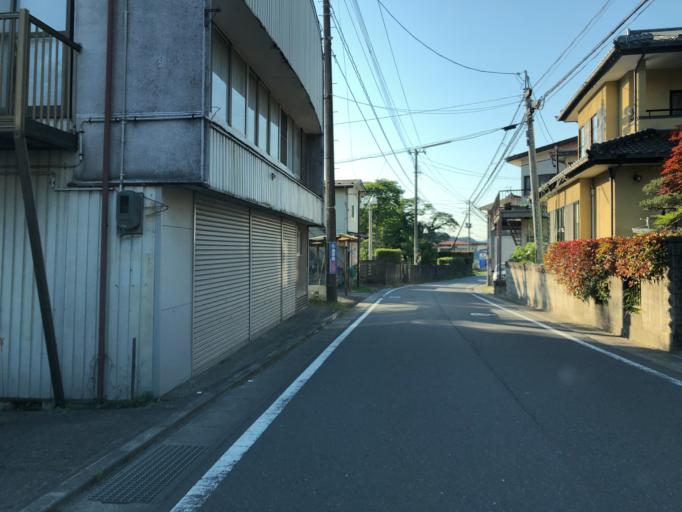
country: JP
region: Ibaraki
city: Daigo
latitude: 36.9364
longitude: 140.4456
